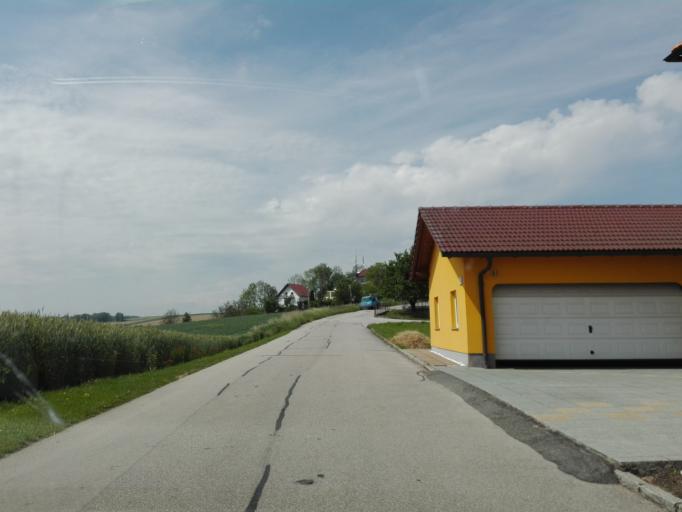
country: AT
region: Upper Austria
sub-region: Politischer Bezirk Perg
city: Perg
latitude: 48.2247
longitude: 14.7063
